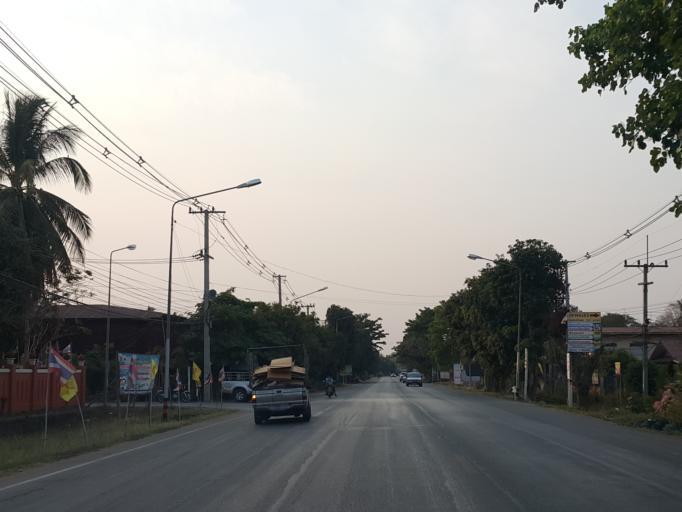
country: TH
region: Sukhothai
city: Si Samrong
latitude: 17.2246
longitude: 99.8603
